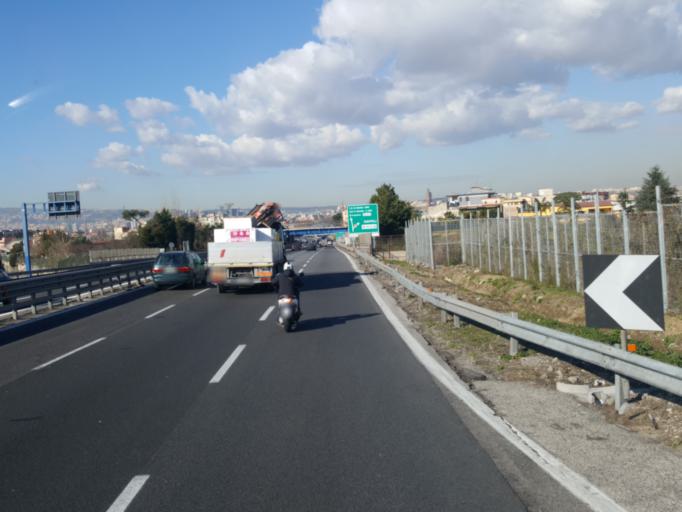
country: IT
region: Campania
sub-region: Provincia di Napoli
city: San Giorgio a Cremano
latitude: 40.8432
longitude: 14.3258
